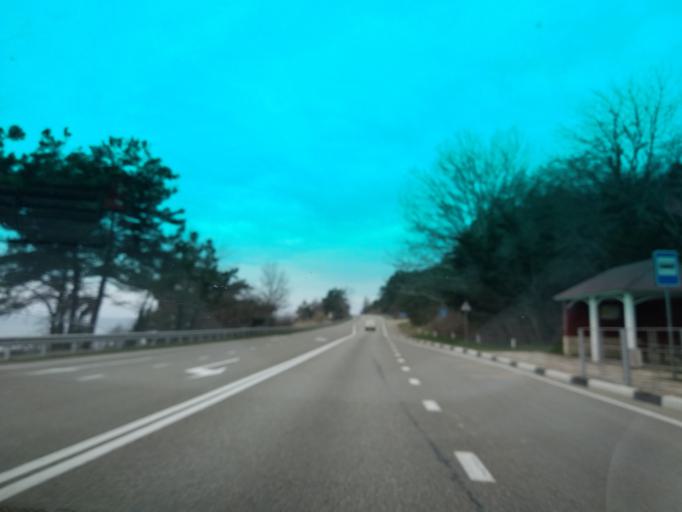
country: RU
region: Krasnodarskiy
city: Ol'ginka
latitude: 44.1865
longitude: 38.9011
